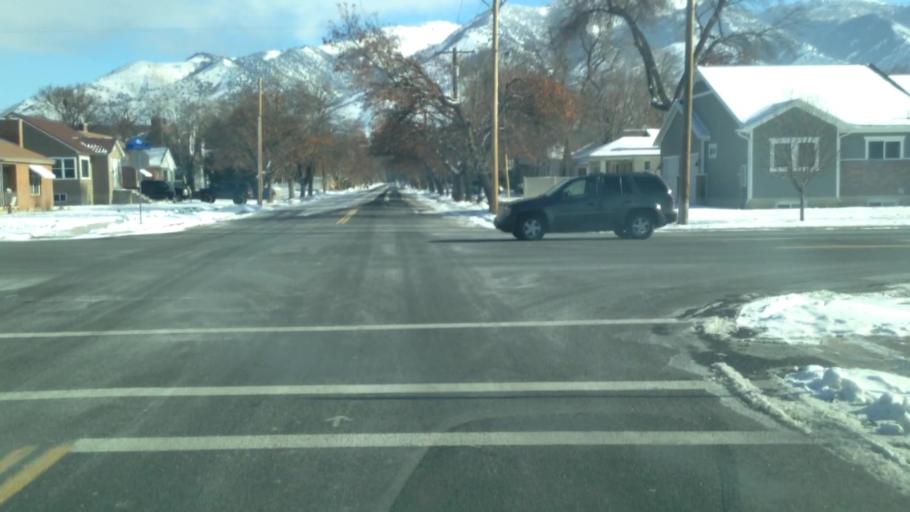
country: US
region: Utah
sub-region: Cache County
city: Logan
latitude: 41.7276
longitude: -111.8302
